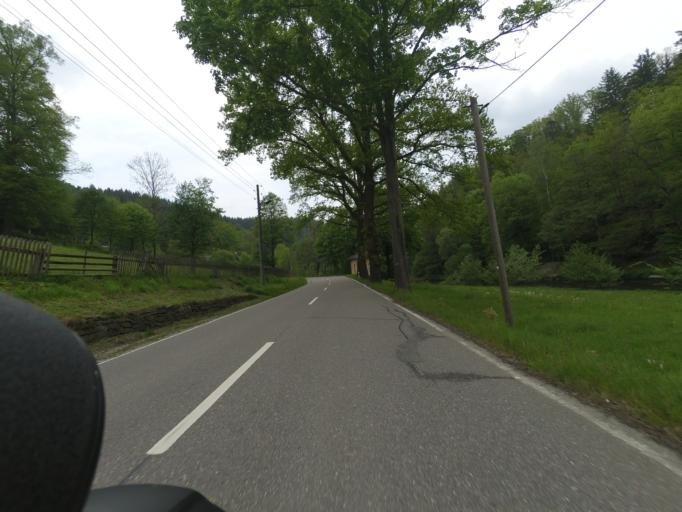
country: DE
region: Saxony
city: Scharfenstein
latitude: 50.6832
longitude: 13.0554
